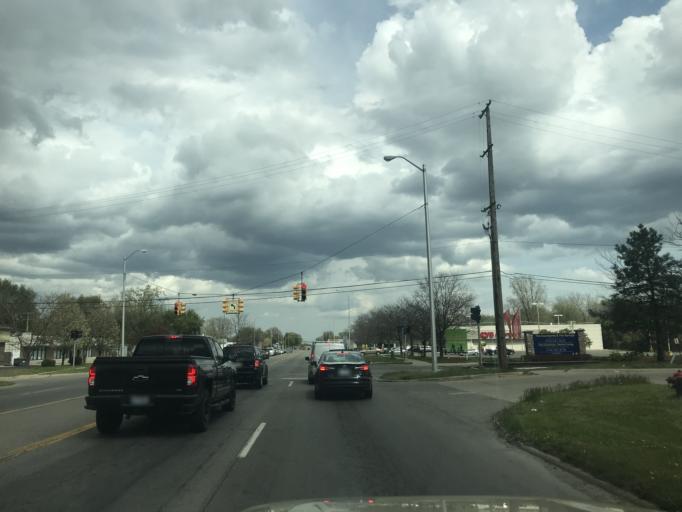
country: US
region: Michigan
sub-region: Wayne County
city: Taylor
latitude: 42.1968
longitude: -83.2926
